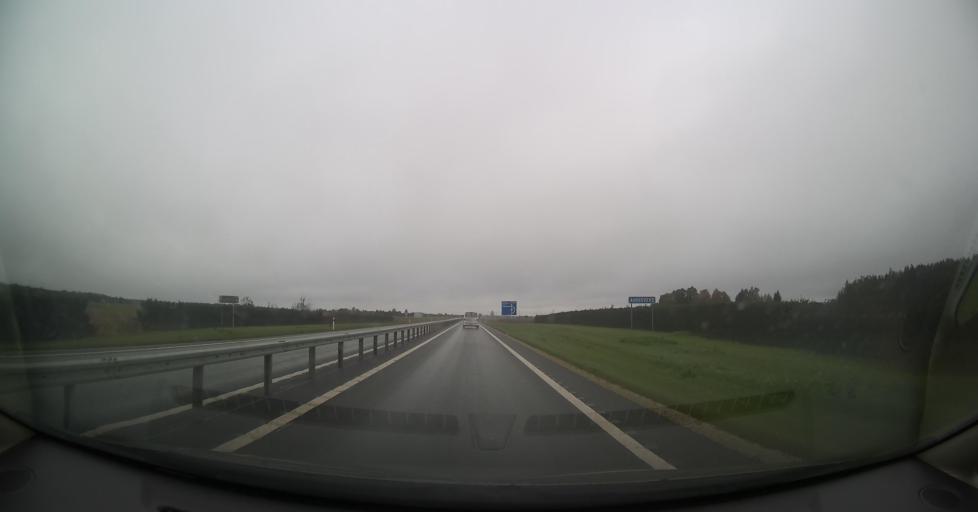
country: EE
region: Jogevamaa
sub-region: Poltsamaa linn
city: Poltsamaa
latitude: 58.6422
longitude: 26.0622
